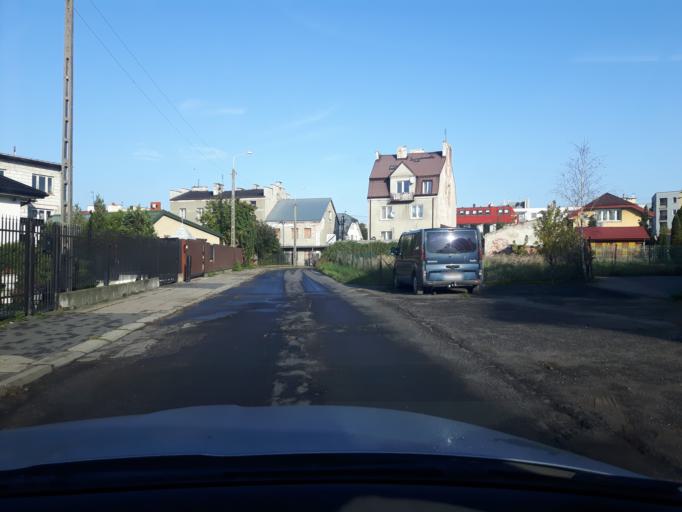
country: PL
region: Masovian Voivodeship
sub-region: Powiat wolominski
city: Zabki
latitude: 52.2880
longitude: 21.1125
